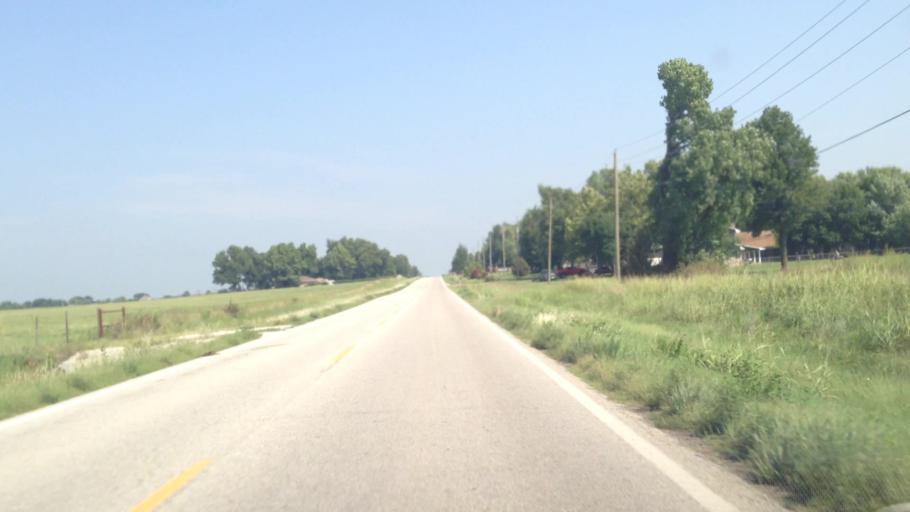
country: US
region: Oklahoma
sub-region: Craig County
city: Vinita
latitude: 36.6625
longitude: -95.1436
